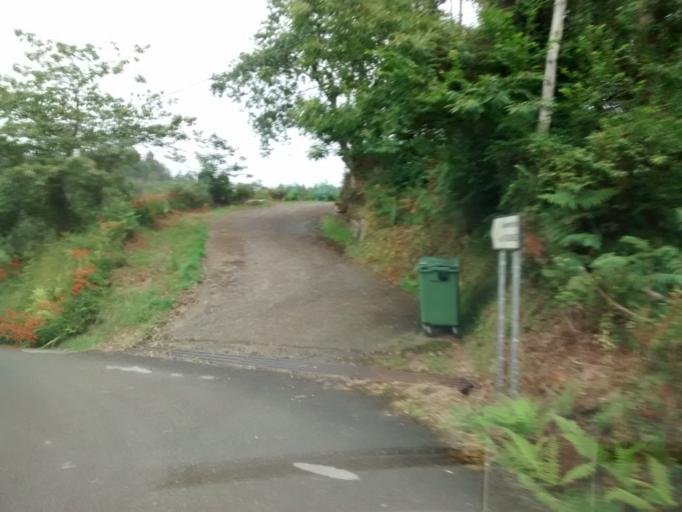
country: ES
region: Asturias
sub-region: Province of Asturias
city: Villaviciosa
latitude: 43.5419
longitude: -5.4083
